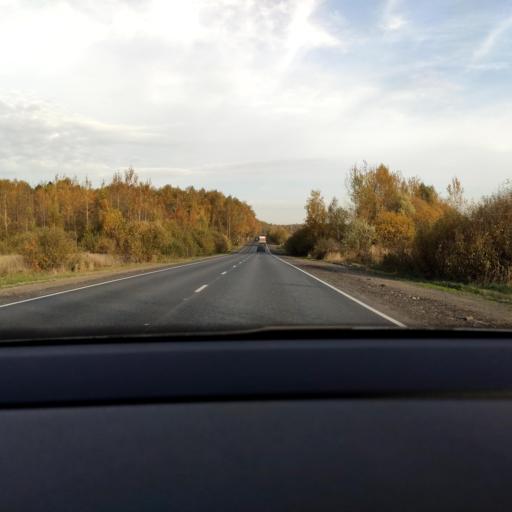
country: RU
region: Moskovskaya
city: Povedniki
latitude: 55.9579
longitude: 37.6397
